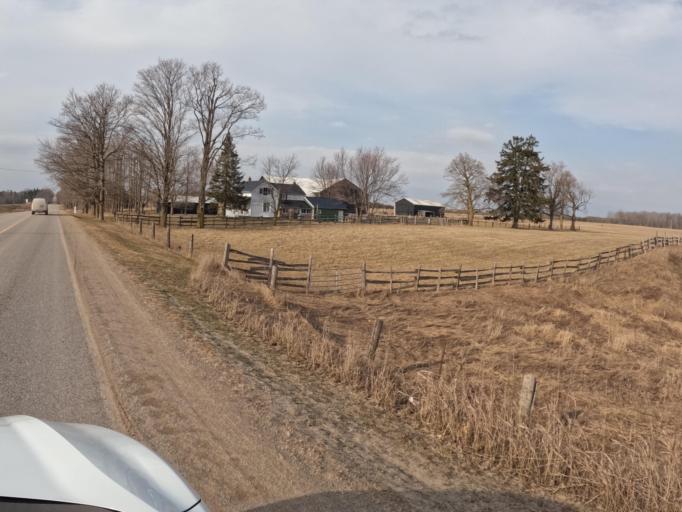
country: CA
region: Ontario
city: Orangeville
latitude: 43.8912
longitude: -80.2657
